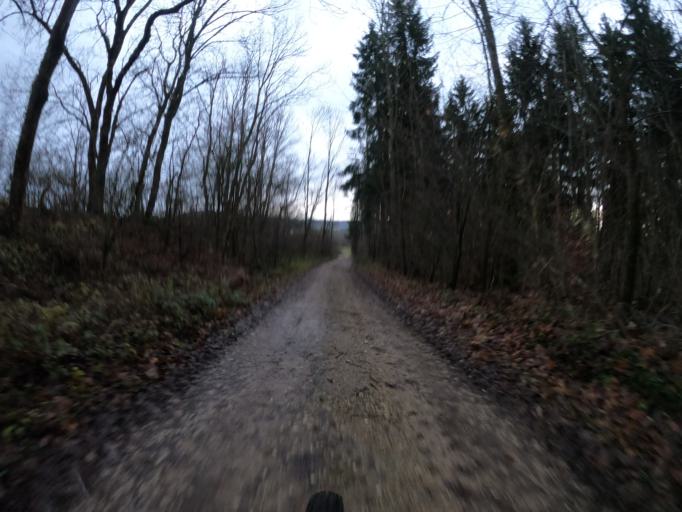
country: DE
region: Baden-Wuerttemberg
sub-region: Regierungsbezirk Stuttgart
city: Sussen
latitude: 48.7024
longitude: 9.7774
